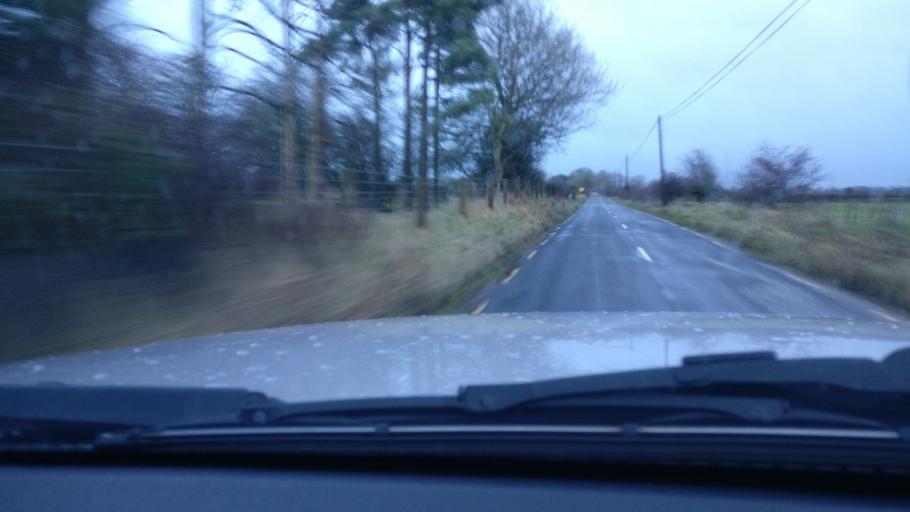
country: IE
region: Connaught
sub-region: County Galway
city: Ballinasloe
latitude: 53.2295
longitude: -8.3239
